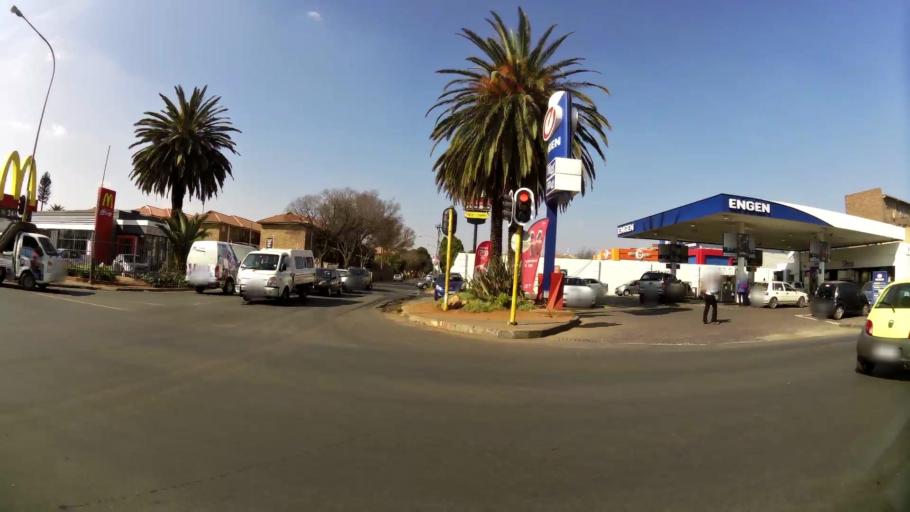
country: ZA
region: Gauteng
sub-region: City of Johannesburg Metropolitan Municipality
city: Modderfontein
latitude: -26.1036
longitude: 28.2324
